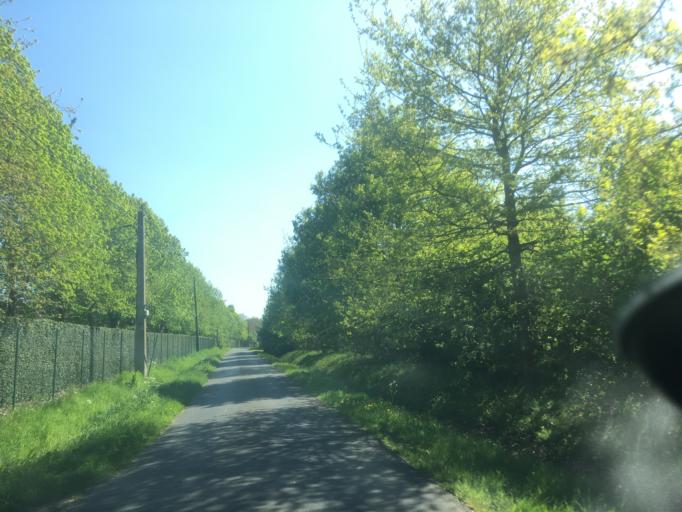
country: BE
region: Flanders
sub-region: Provincie West-Vlaanderen
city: Ardooie
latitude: 50.9588
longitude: 3.2192
